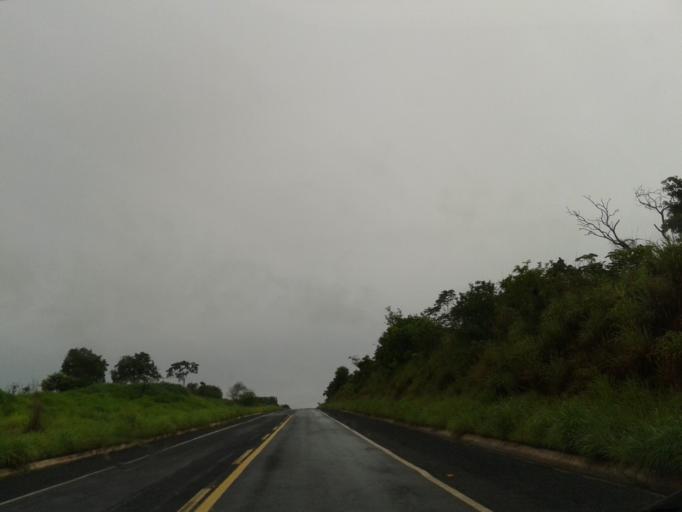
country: BR
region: Minas Gerais
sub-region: Santa Vitoria
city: Santa Vitoria
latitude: -19.1207
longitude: -50.2980
